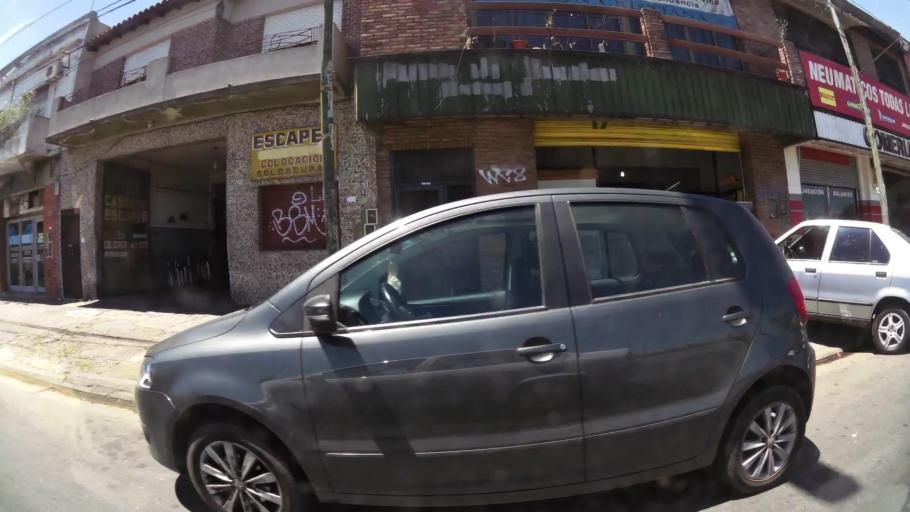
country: AR
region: Buenos Aires
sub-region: Partido de San Isidro
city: San Isidro
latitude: -34.5050
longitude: -58.5627
